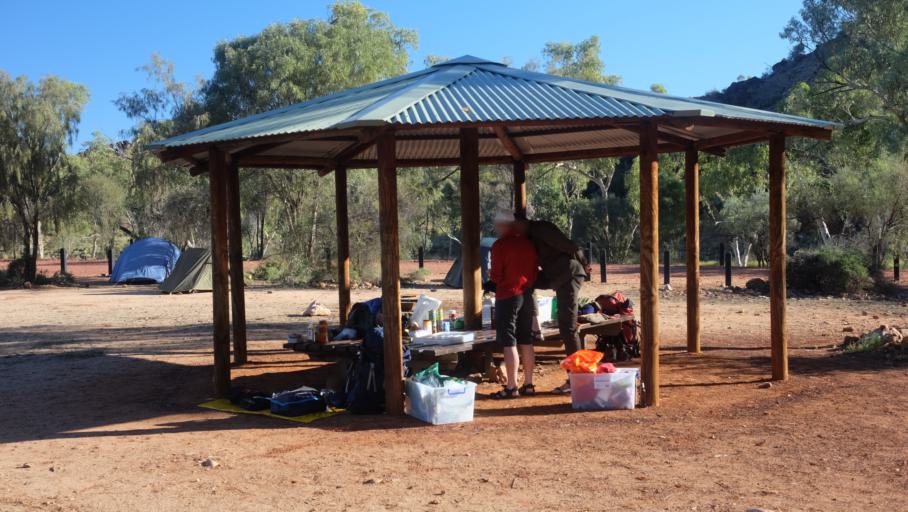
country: AU
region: Northern Territory
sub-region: Alice Springs
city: Alice Springs
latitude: -23.7801
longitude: 133.0726
